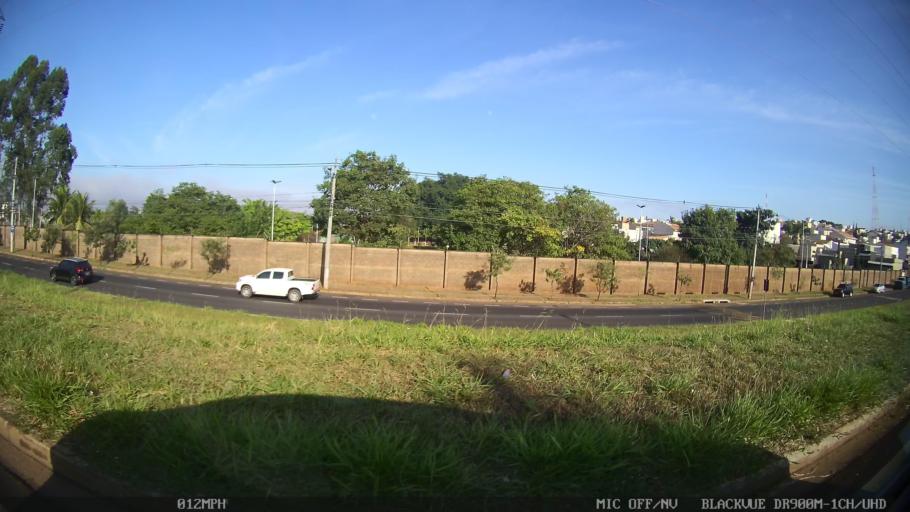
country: BR
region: Sao Paulo
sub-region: Sao Jose Do Rio Preto
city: Sao Jose do Rio Preto
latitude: -20.8070
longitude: -49.3428
